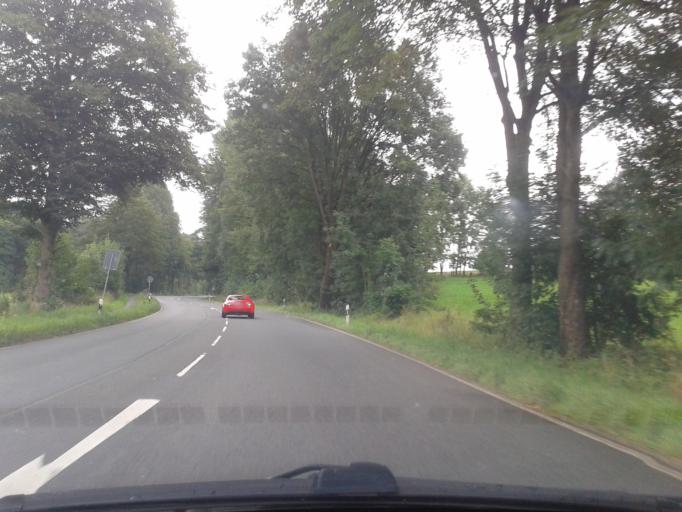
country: DE
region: North Rhine-Westphalia
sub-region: Regierungsbezirk Detmold
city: Horn
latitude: 51.8965
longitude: 8.9374
